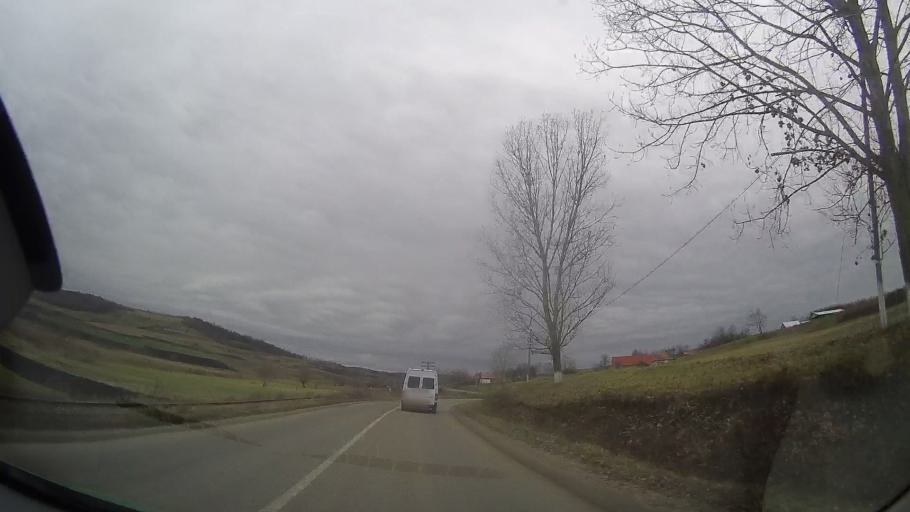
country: RO
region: Cluj
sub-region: Comuna Catina
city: Catina
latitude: 46.7995
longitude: 24.2139
